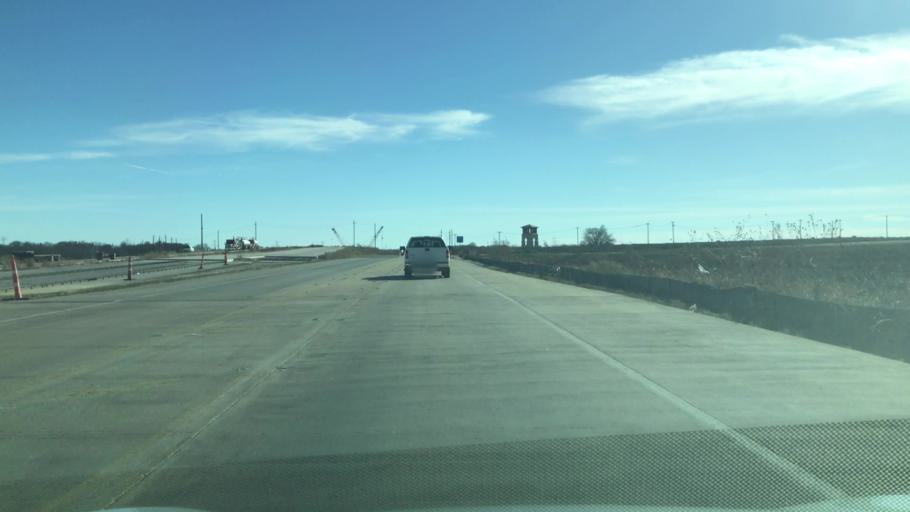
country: US
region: Texas
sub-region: Tarrant County
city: Mansfield
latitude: 32.5504
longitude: -97.0855
